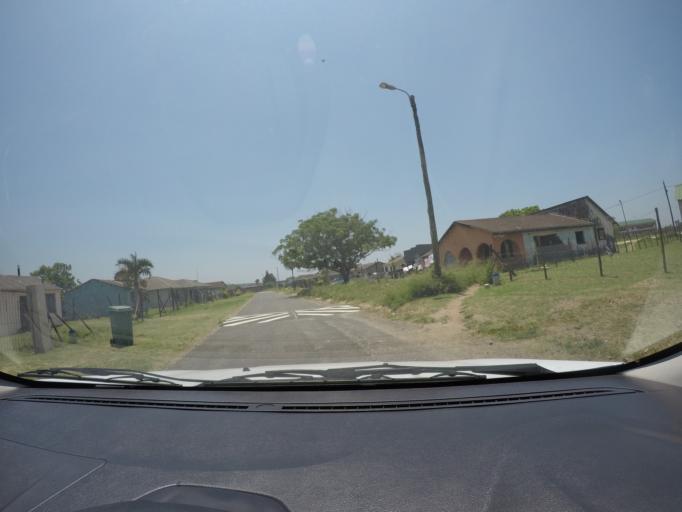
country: ZA
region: KwaZulu-Natal
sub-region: uThungulu District Municipality
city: eSikhawini
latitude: -28.8832
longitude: 31.9027
